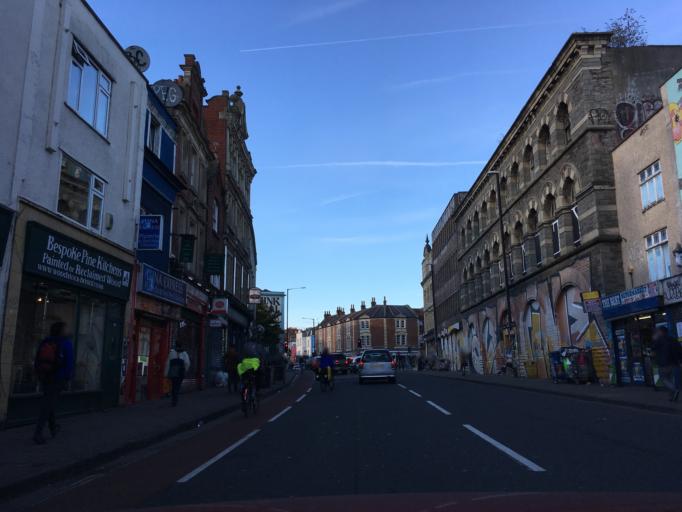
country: GB
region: England
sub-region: Bristol
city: Bristol
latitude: 51.4634
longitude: -2.5898
